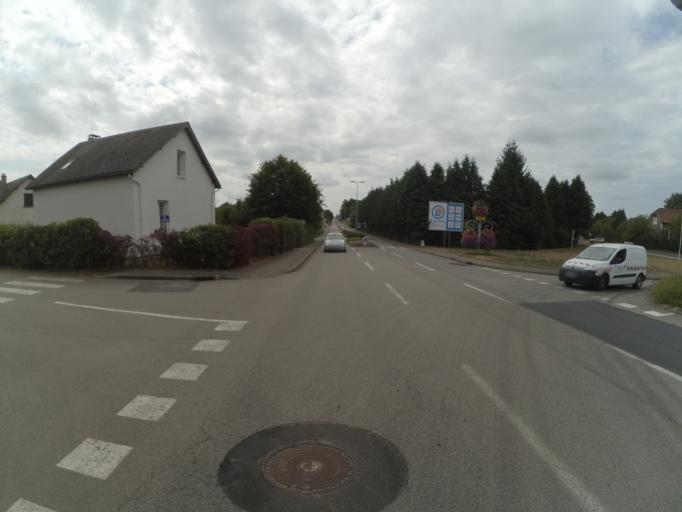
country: FR
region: Limousin
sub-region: Departement de la Correze
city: Ussel
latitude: 45.5636
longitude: 2.3001
